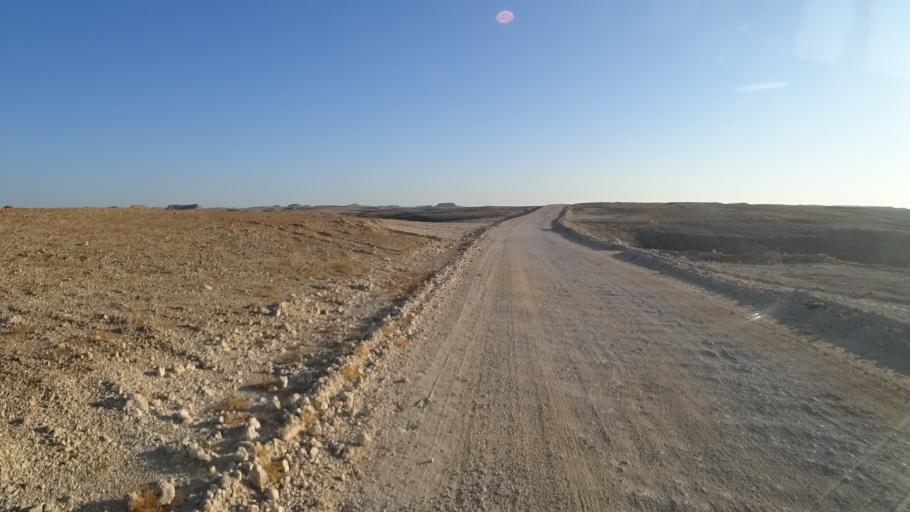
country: YE
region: Al Mahrah
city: Hawf
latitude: 17.1603
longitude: 53.3507
